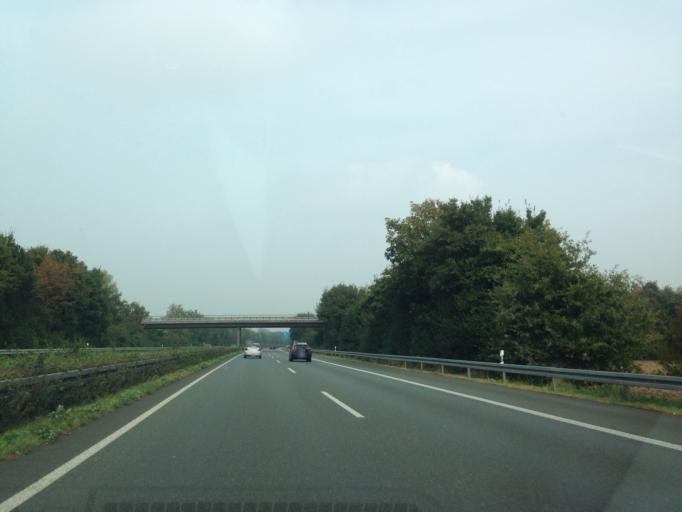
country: DE
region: North Rhine-Westphalia
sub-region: Regierungsbezirk Munster
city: Nottuln
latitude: 51.8986
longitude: 7.3831
